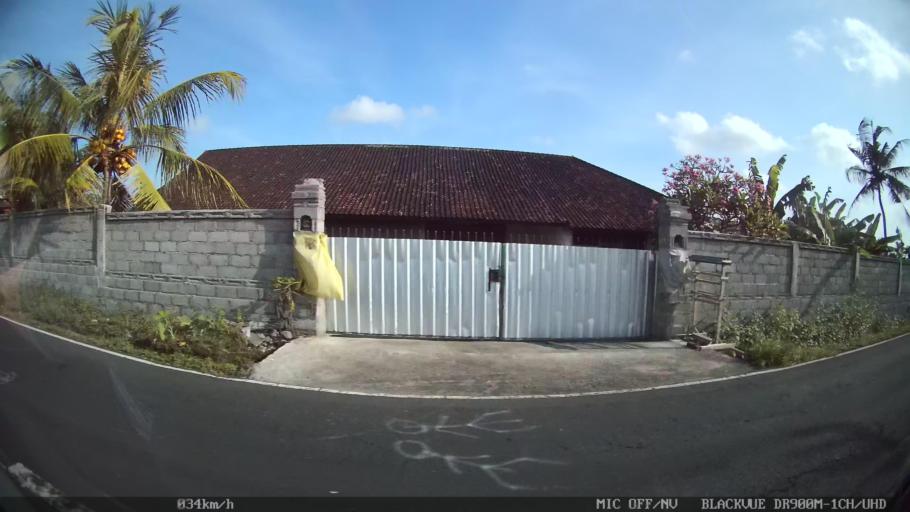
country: ID
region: Bali
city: Banjar Desa
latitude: -8.5797
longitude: 115.2330
